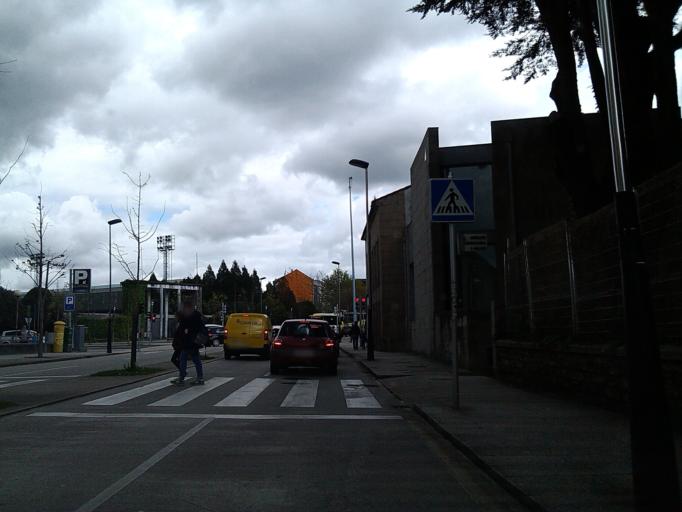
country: ES
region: Galicia
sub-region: Provincia da Coruna
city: Santiago de Compostela
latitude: 42.8840
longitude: -8.5482
